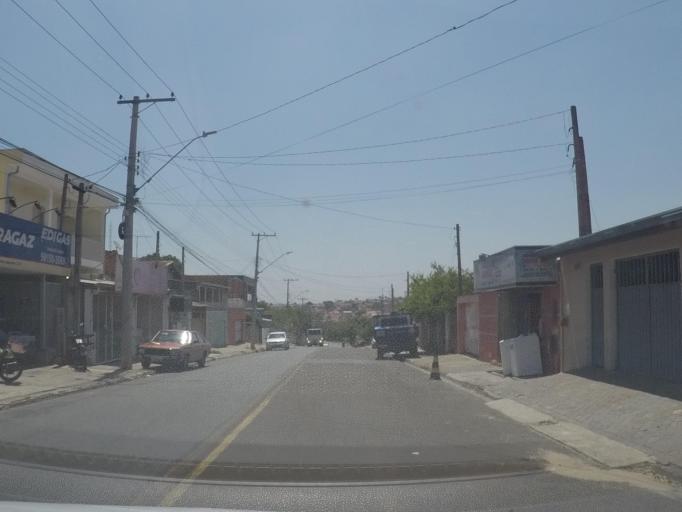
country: BR
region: Sao Paulo
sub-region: Hortolandia
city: Hortolandia
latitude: -22.8583
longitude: -47.2041
